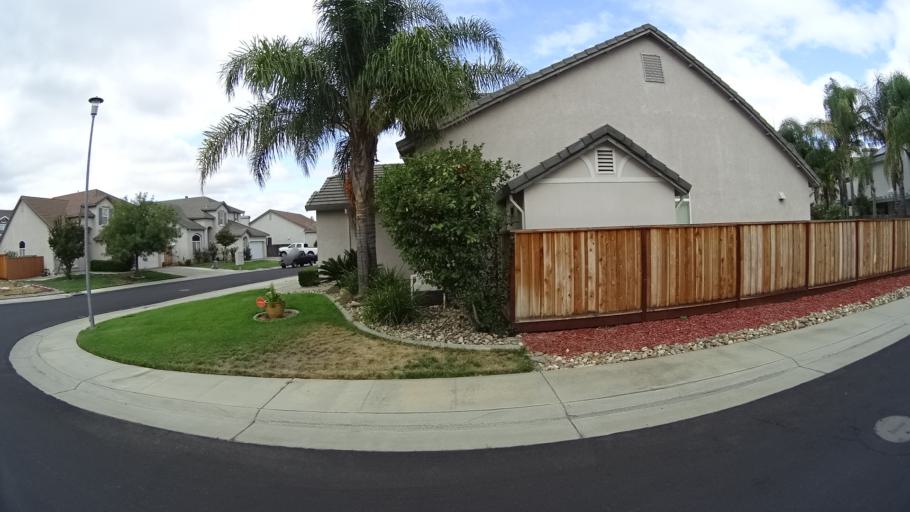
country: US
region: California
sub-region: Sacramento County
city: Laguna
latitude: 38.4108
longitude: -121.4223
